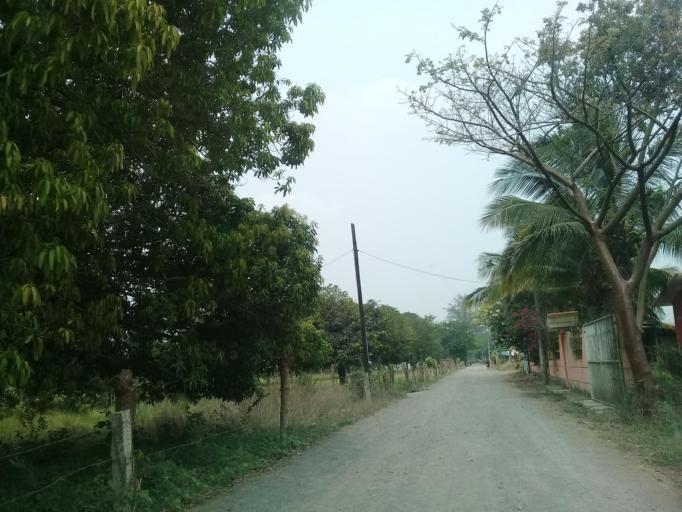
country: MX
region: Veracruz
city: Jamapa
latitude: 18.9520
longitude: -96.2018
